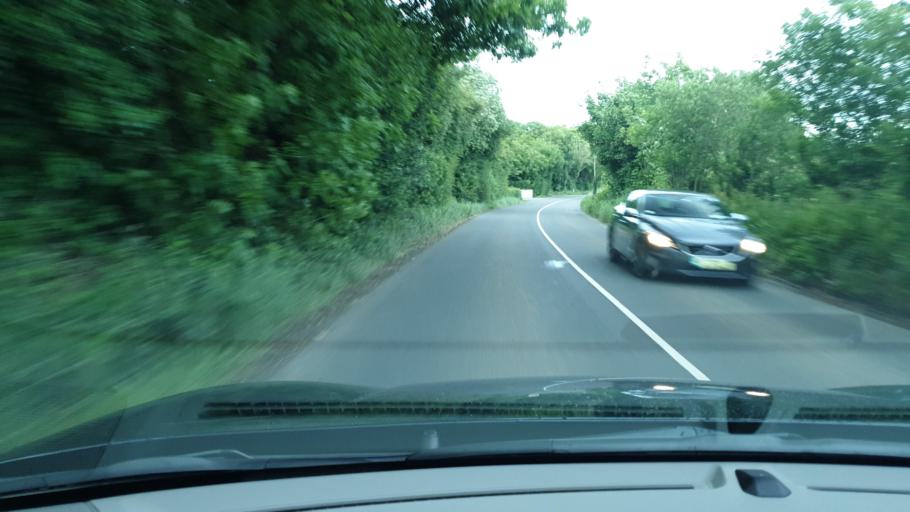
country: IE
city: Kentstown
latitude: 53.5939
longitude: -6.4993
